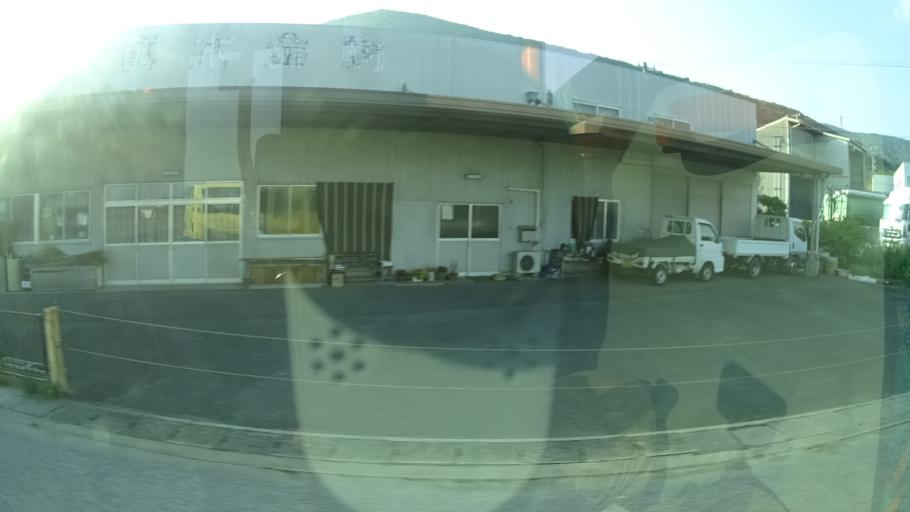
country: JP
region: Aichi
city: Tahara
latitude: 34.6512
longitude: 137.2263
